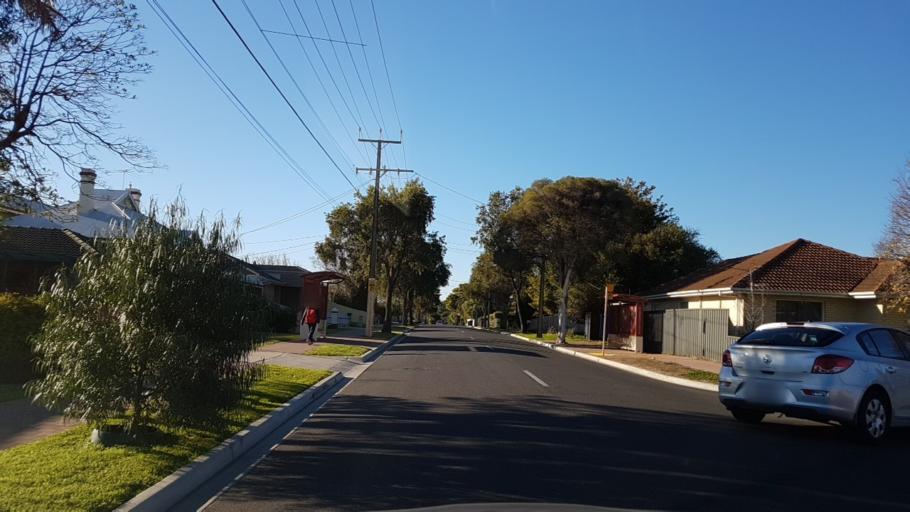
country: AU
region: South Australia
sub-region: Campbelltown
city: Campbelltown
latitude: -34.8795
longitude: 138.6561
